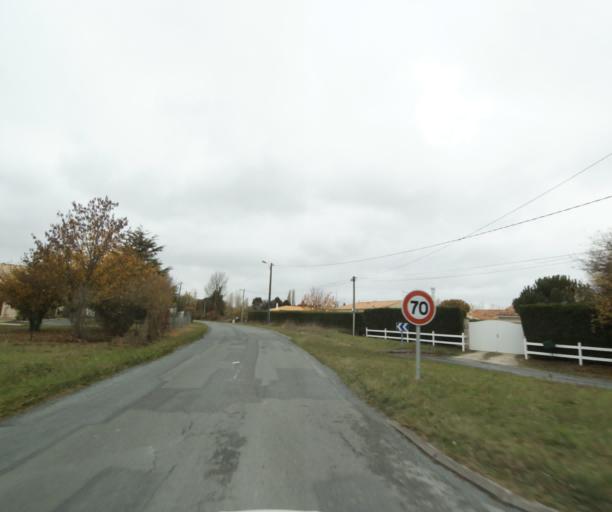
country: FR
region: Poitou-Charentes
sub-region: Departement de la Charente-Maritime
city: Fontcouverte
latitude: 45.7625
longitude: -0.5790
